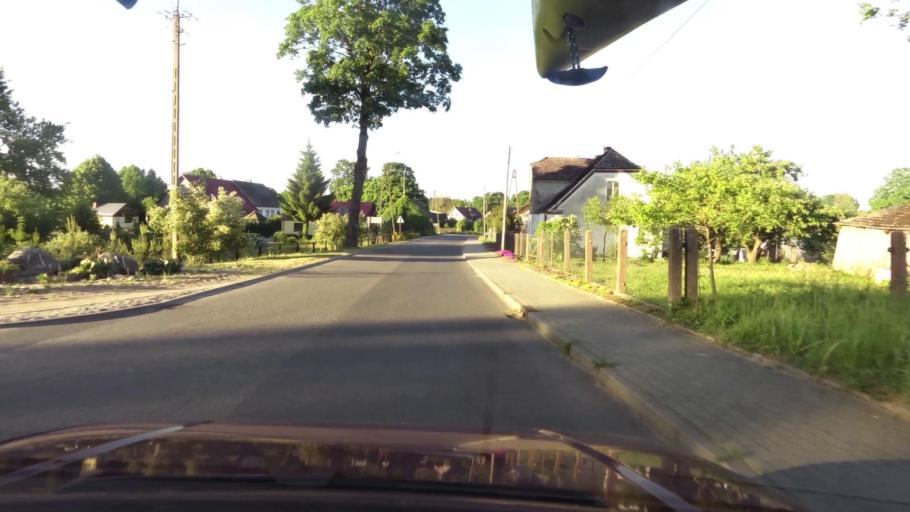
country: PL
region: West Pomeranian Voivodeship
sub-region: Powiat szczecinecki
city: Bialy Bor
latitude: 53.9484
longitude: 16.7748
